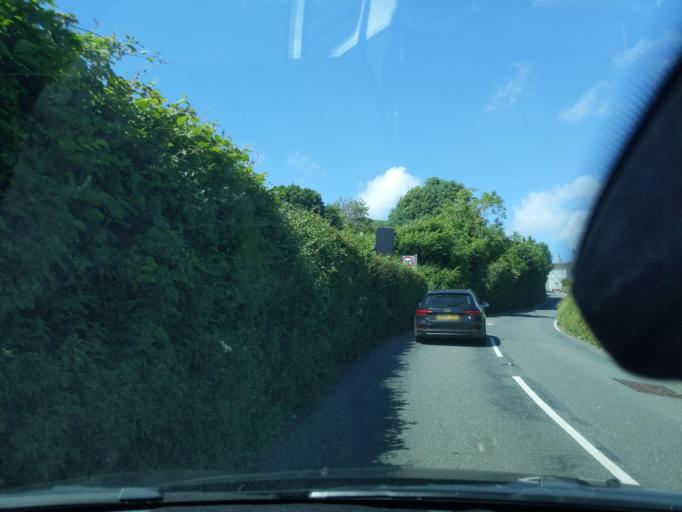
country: GB
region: England
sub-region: Devon
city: Fremington
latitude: 51.0468
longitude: -4.0924
